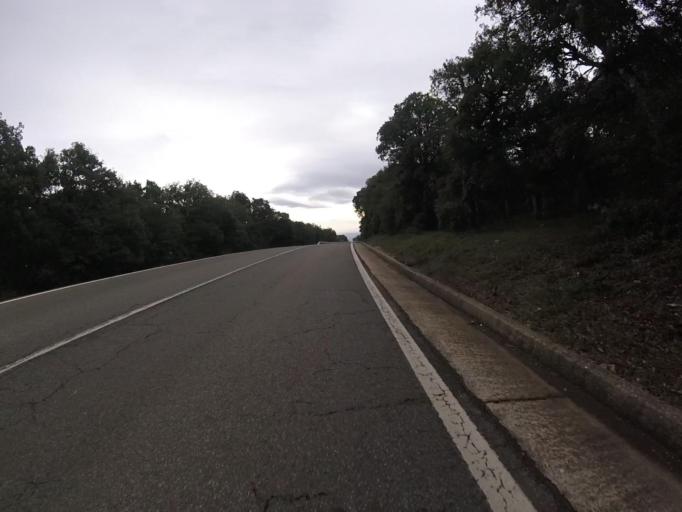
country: ES
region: Navarre
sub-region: Provincia de Navarra
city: Lezaun
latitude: 42.7570
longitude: -2.0116
